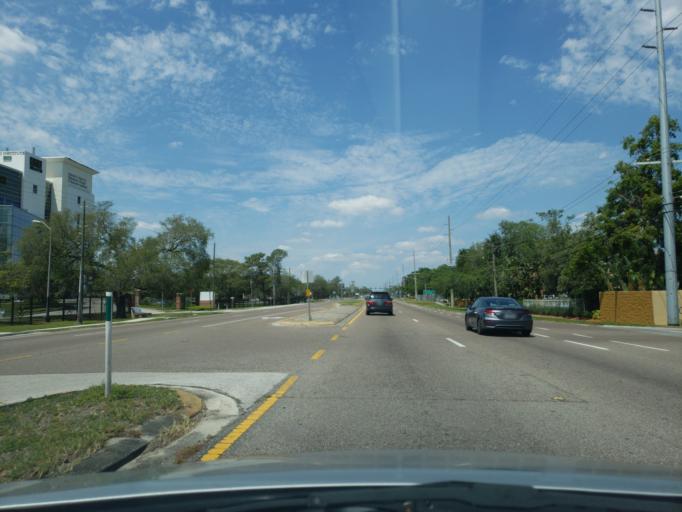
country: US
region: Florida
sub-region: Hillsborough County
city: University
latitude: 28.0692
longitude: -82.4166
